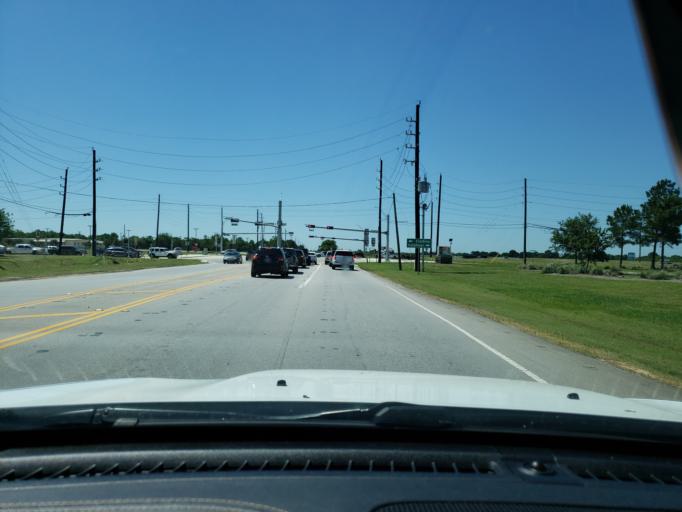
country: US
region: Texas
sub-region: Fort Bend County
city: Fulshear
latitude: 29.6959
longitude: -95.8460
